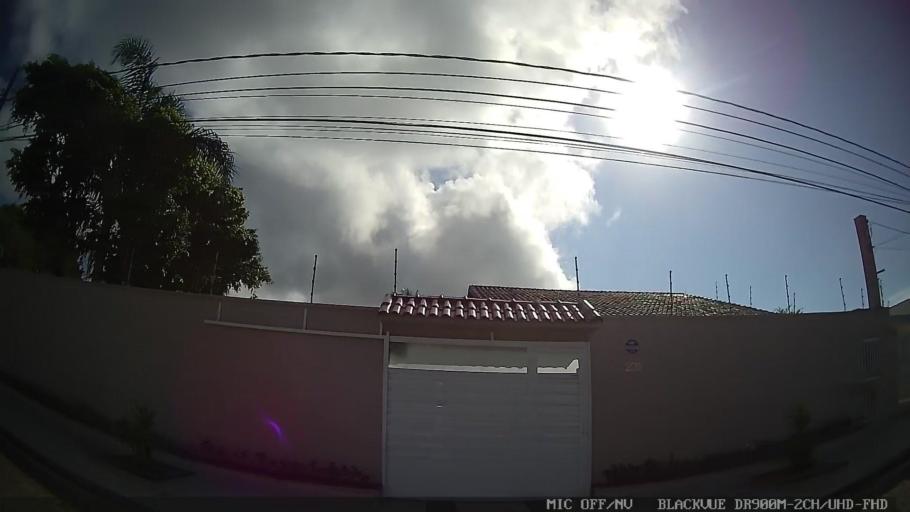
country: BR
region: Sao Paulo
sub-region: Peruibe
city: Peruibe
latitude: -24.2737
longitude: -46.9380
